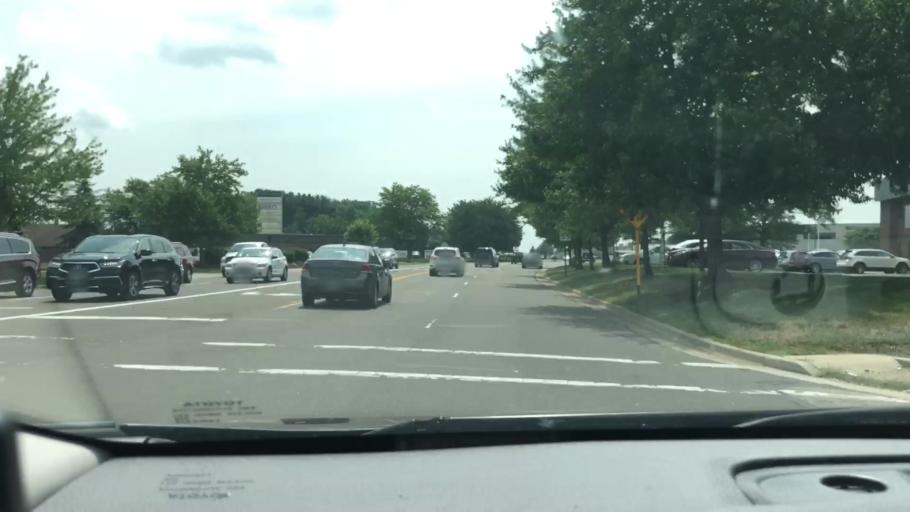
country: US
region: Ohio
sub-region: Stark County
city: North Canton
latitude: 40.8480
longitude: -81.4345
